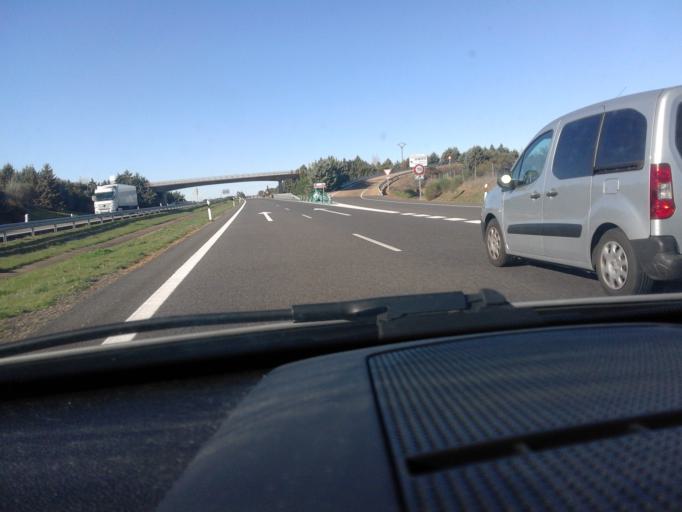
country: ES
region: Castille and Leon
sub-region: Provincia de Leon
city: Calzada del Coto
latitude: 42.3832
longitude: -5.0745
